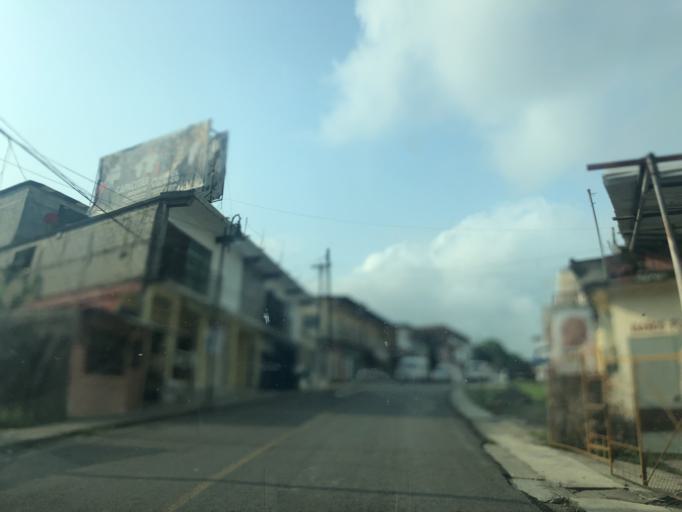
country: MX
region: Chiapas
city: Pichucalco
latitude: 17.5084
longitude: -93.1168
